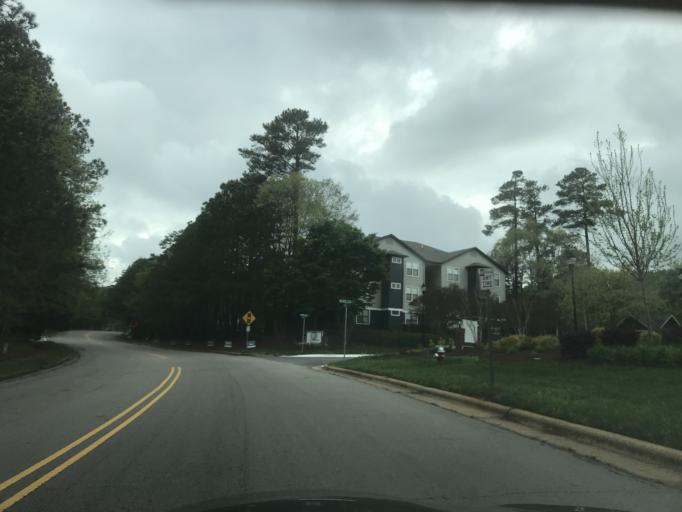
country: US
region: North Carolina
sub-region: Wake County
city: West Raleigh
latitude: 35.7505
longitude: -78.6926
